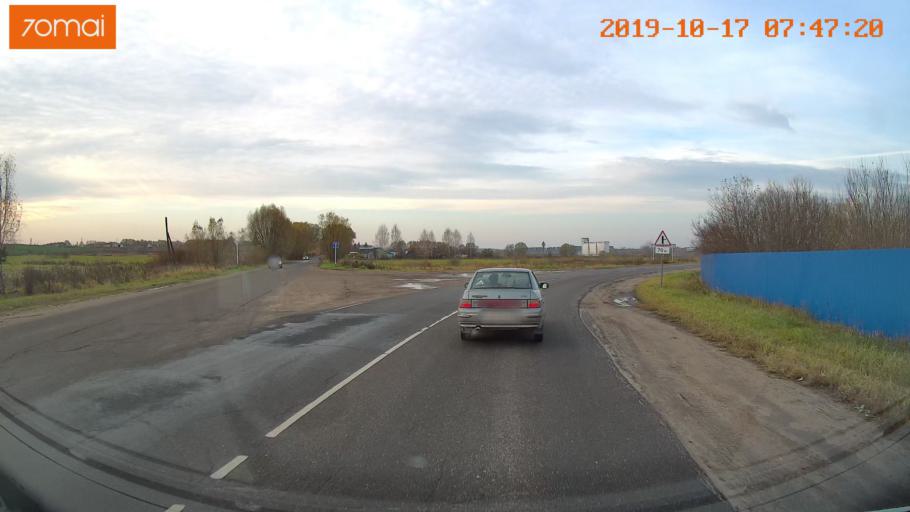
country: RU
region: Vladimir
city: Yur'yev-Pol'skiy
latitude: 56.4882
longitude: 39.6864
